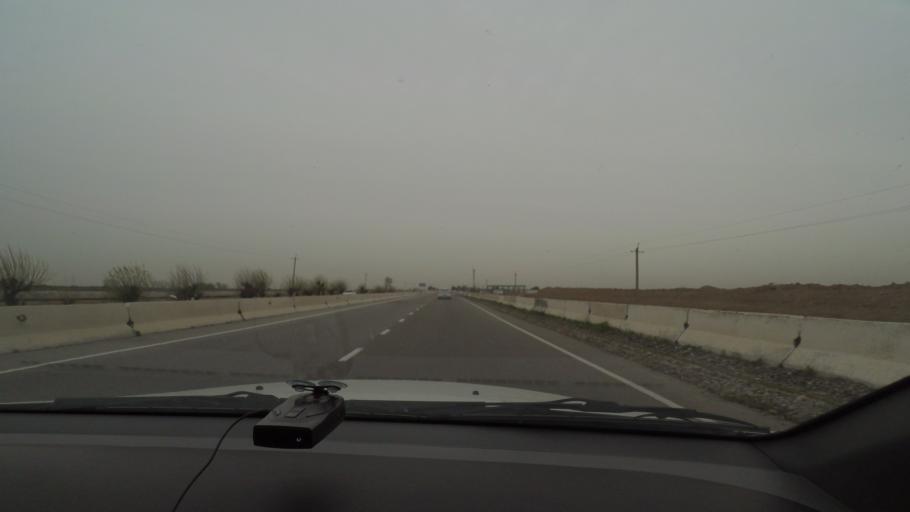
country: UZ
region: Jizzax
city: Gagarin
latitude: 40.4674
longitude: 68.2692
